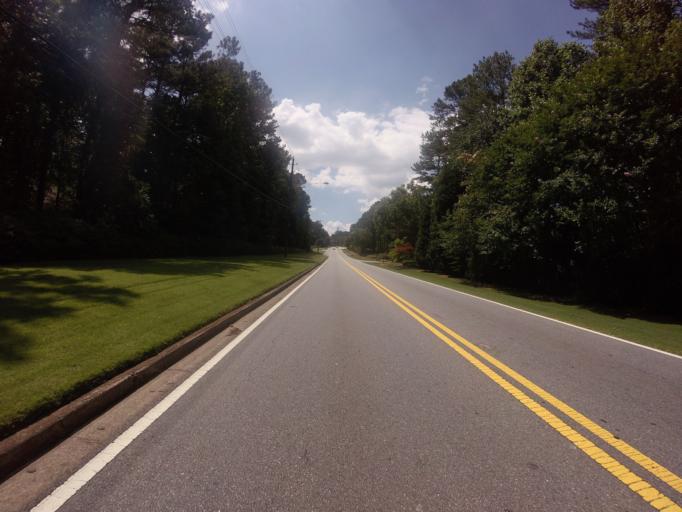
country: US
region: Georgia
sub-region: Fulton County
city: Johns Creek
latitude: 34.0216
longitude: -84.2477
